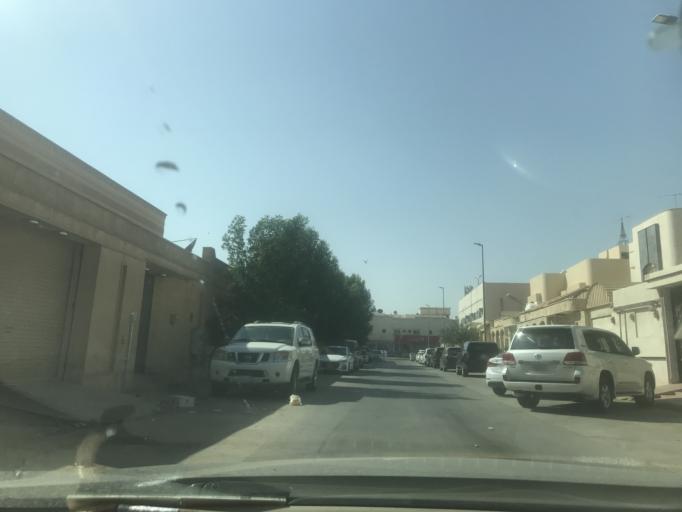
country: SA
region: Ar Riyad
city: Riyadh
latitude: 24.7412
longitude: 46.7598
